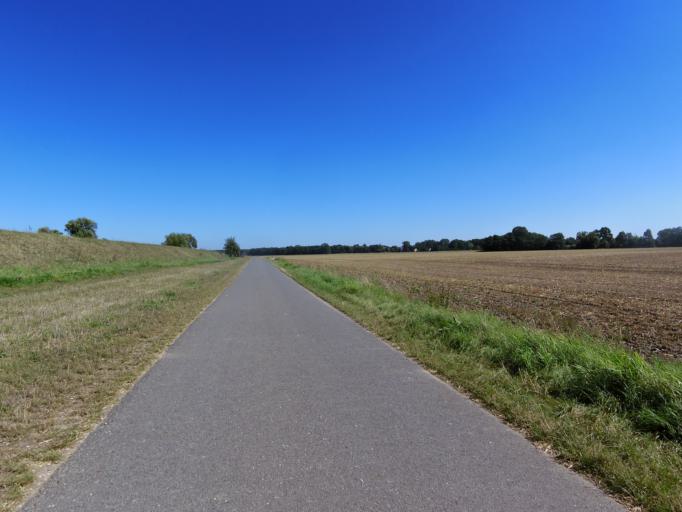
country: DE
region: Saxony-Anhalt
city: Pretzsch
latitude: 51.7388
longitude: 12.8212
